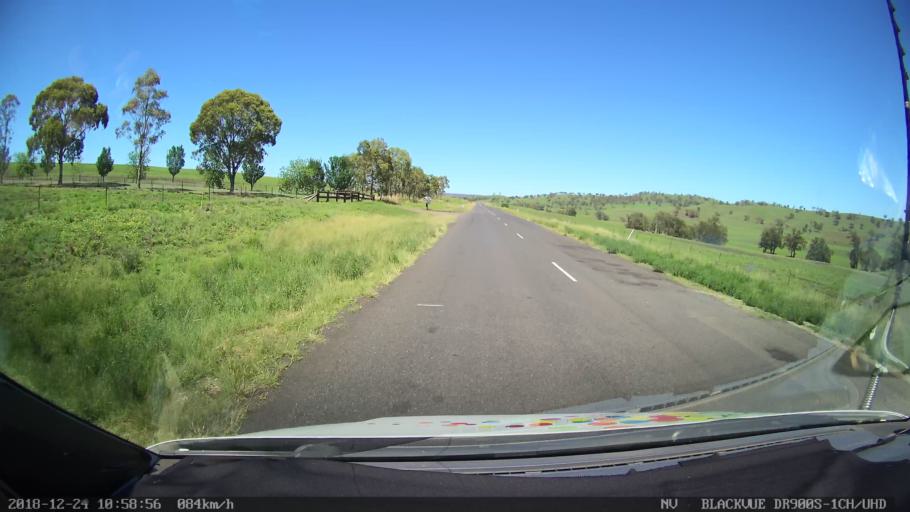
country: AU
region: New South Wales
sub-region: Upper Hunter Shire
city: Merriwa
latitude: -32.0530
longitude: 150.4037
